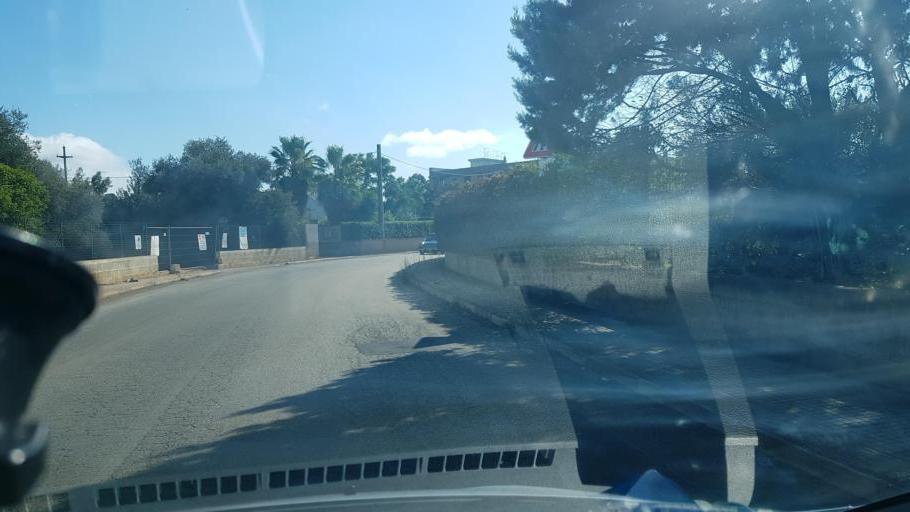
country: IT
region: Apulia
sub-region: Provincia di Brindisi
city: San Vito dei Normanni
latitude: 40.6587
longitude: 17.7175
